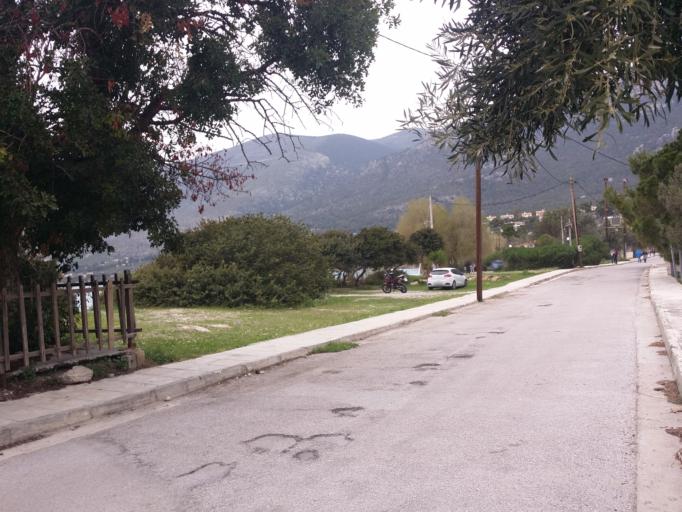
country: GR
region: Central Greece
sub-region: Nomos Voiotias
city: Kaparellion
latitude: 38.1486
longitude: 23.2251
